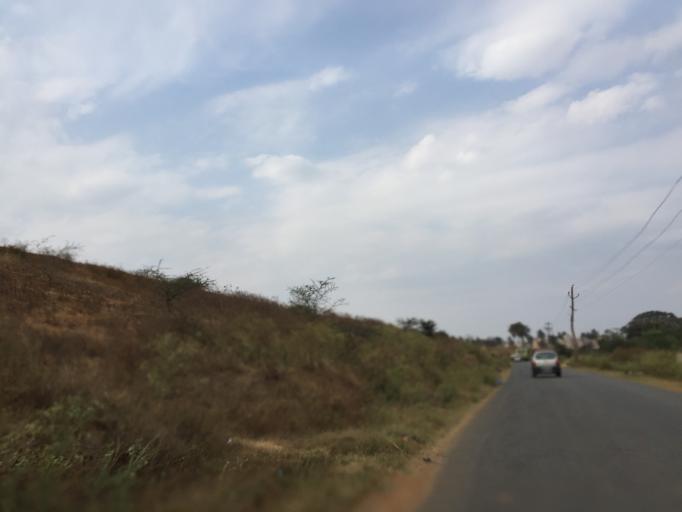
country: IN
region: Karnataka
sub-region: Chikkaballapur
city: Chik Ballapur
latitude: 13.4242
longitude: 77.7212
